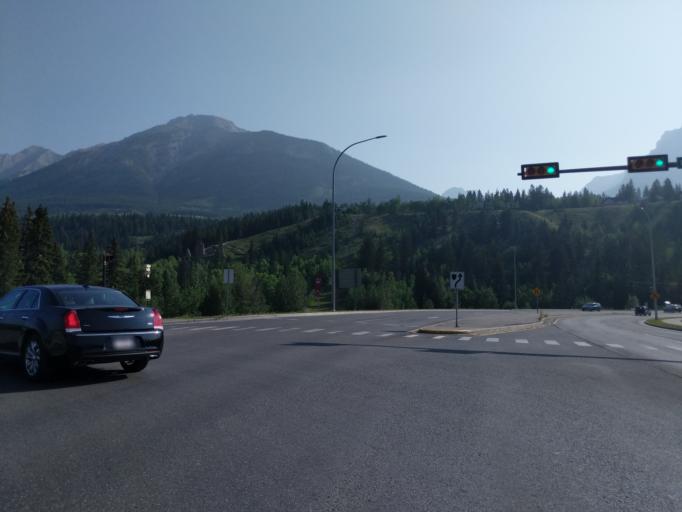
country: CA
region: Alberta
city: Canmore
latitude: 51.0904
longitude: -115.3432
